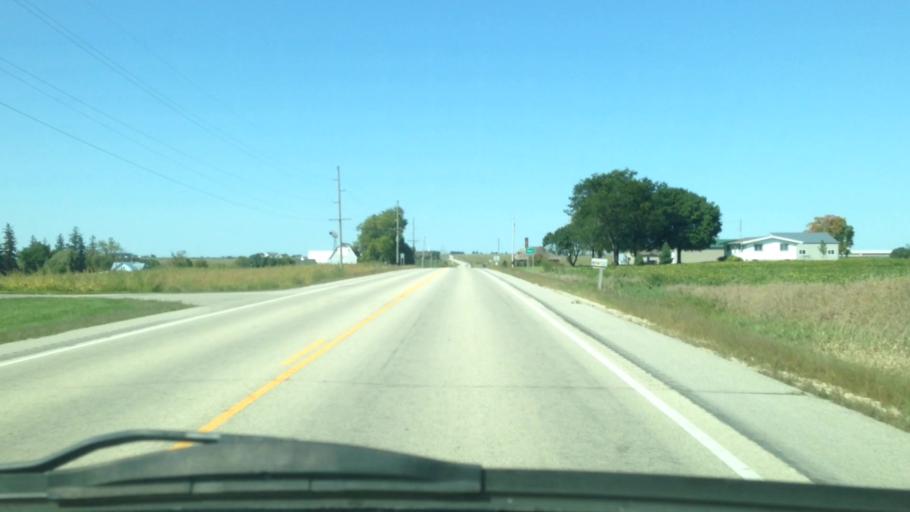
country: US
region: Minnesota
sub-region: Fillmore County
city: Rushford
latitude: 43.8724
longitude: -91.7396
